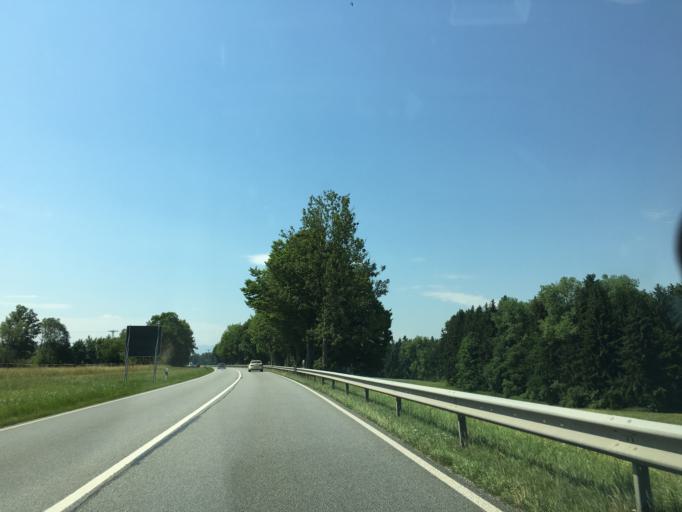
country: DE
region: Bavaria
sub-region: Upper Bavaria
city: Edling
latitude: 48.0387
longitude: 12.1795
